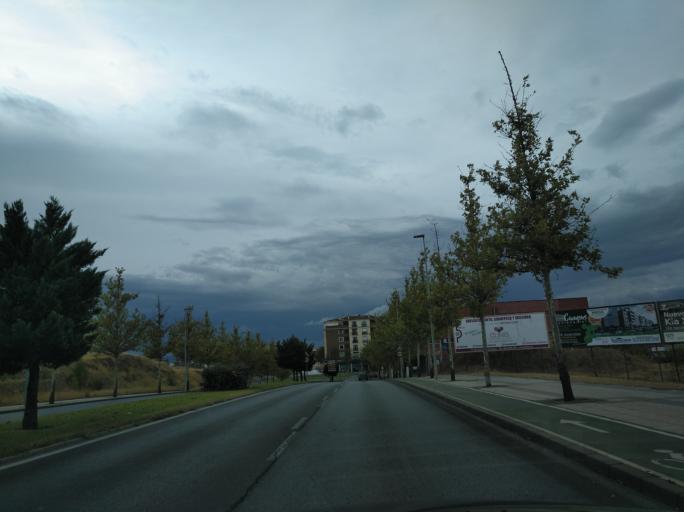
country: ES
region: Extremadura
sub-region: Provincia de Badajoz
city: Badajoz
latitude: 38.8634
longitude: -6.9750
